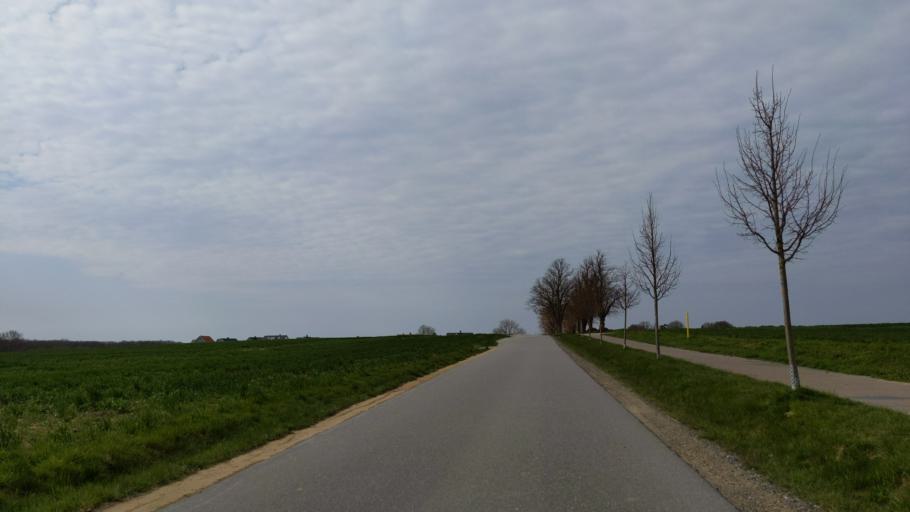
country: DE
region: Mecklenburg-Vorpommern
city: Dassow
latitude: 53.9619
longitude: 10.9702
